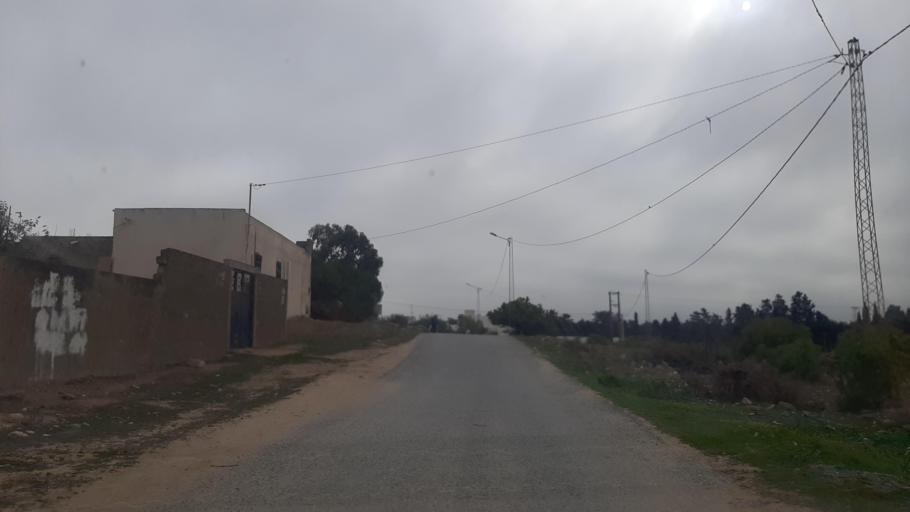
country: TN
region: Nabul
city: Menzel Heurr
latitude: 36.6716
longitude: 10.9186
